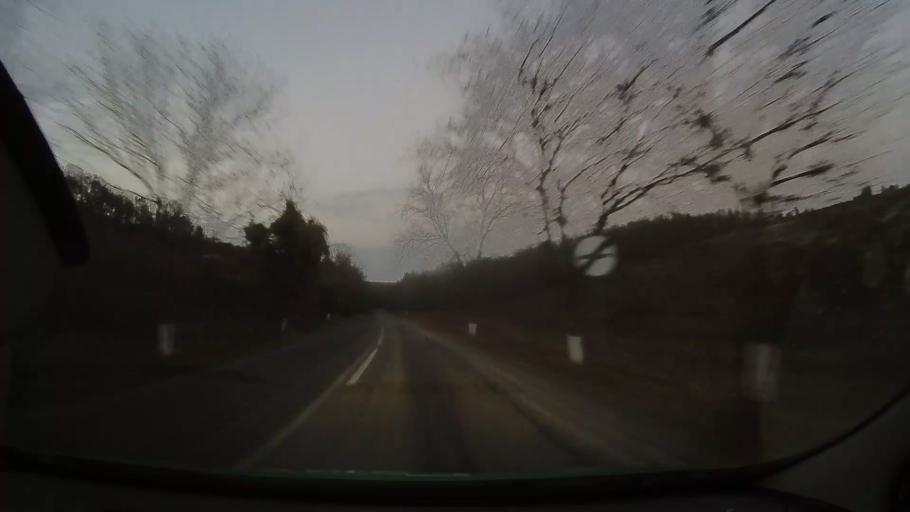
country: RO
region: Constanta
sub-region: Comuna Baneasa
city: Baneasa
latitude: 44.0771
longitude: 27.7383
